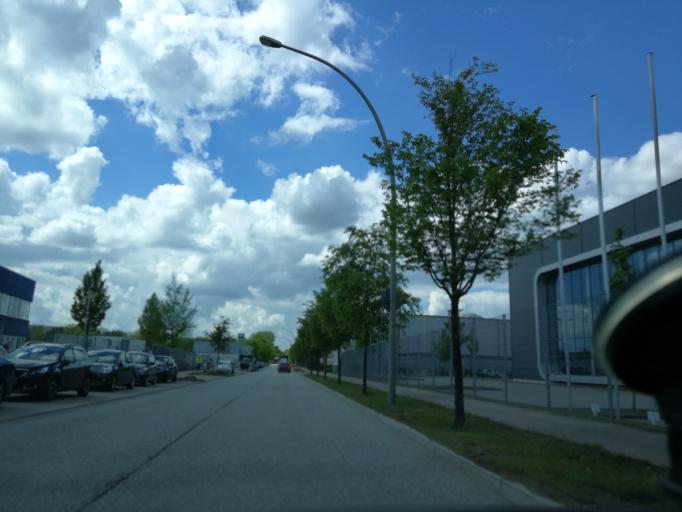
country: DE
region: Hamburg
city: Altona
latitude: 53.4787
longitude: 9.9085
